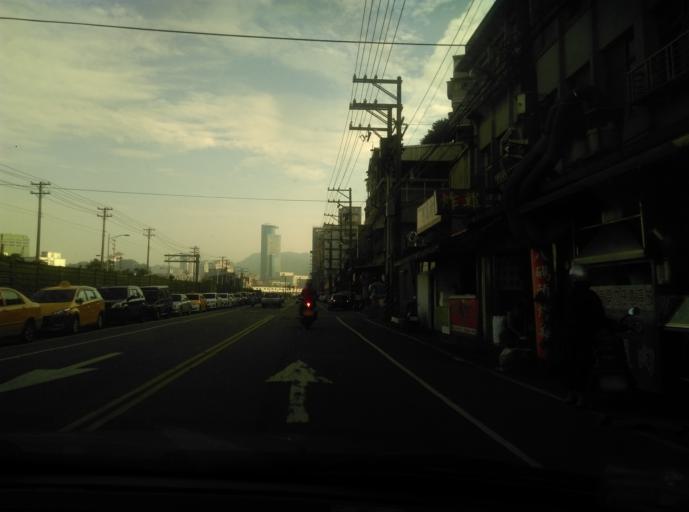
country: TW
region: Taiwan
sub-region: Keelung
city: Keelung
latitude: 25.1403
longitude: 121.7397
